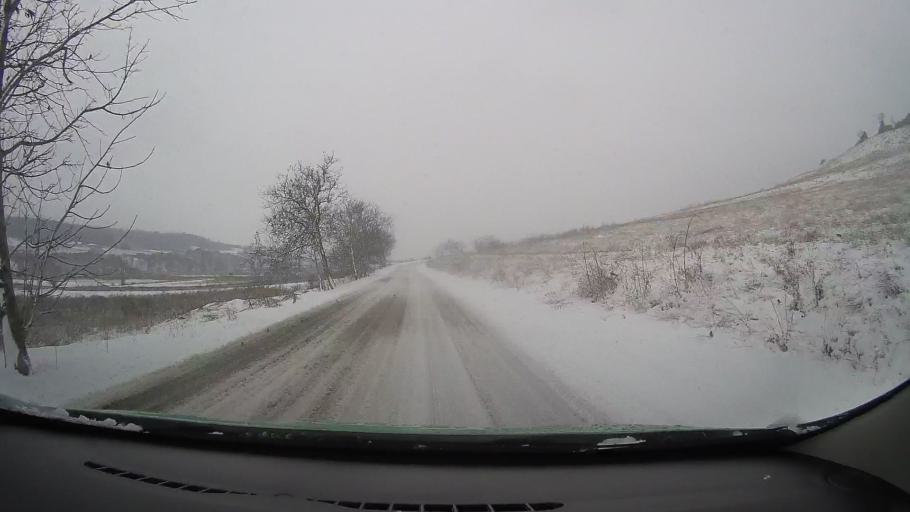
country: RO
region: Hunedoara
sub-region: Comuna Pestisu Mic
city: Pestisu Mic
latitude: 45.7977
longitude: 22.8973
